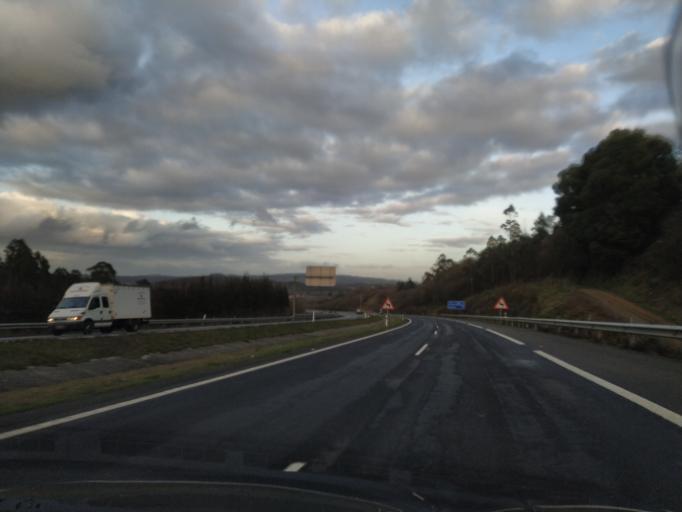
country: ES
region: Galicia
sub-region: Provincia da Coruna
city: Santiago de Compostela
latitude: 42.8964
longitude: -8.4744
